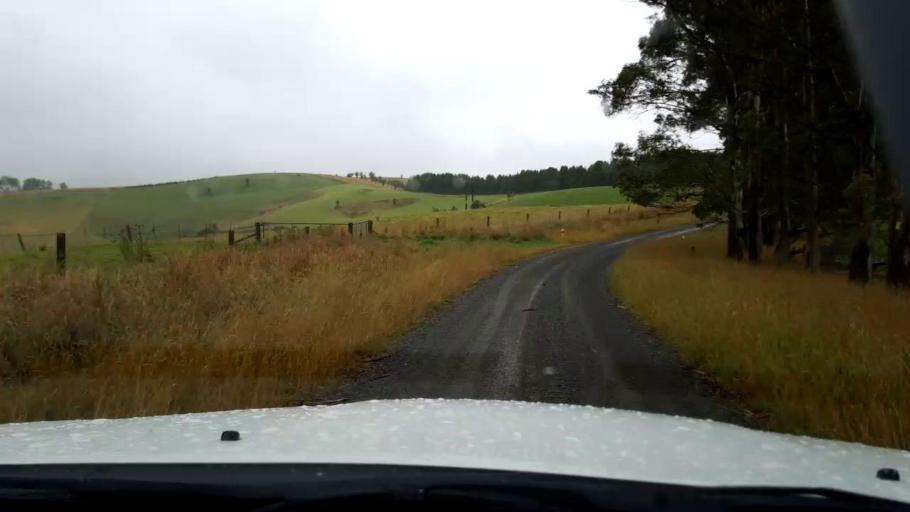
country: NZ
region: Canterbury
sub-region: Timaru District
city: Pleasant Point
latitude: -44.1731
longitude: 171.1008
